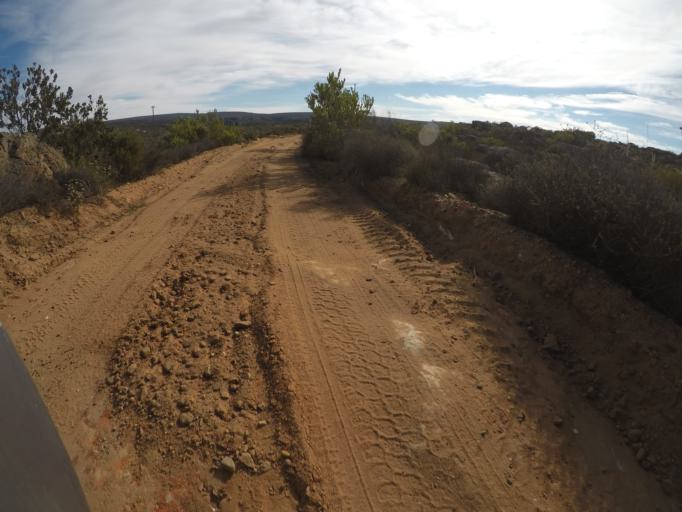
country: ZA
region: Western Cape
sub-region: West Coast District Municipality
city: Vredendal
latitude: -31.7482
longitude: 18.8232
